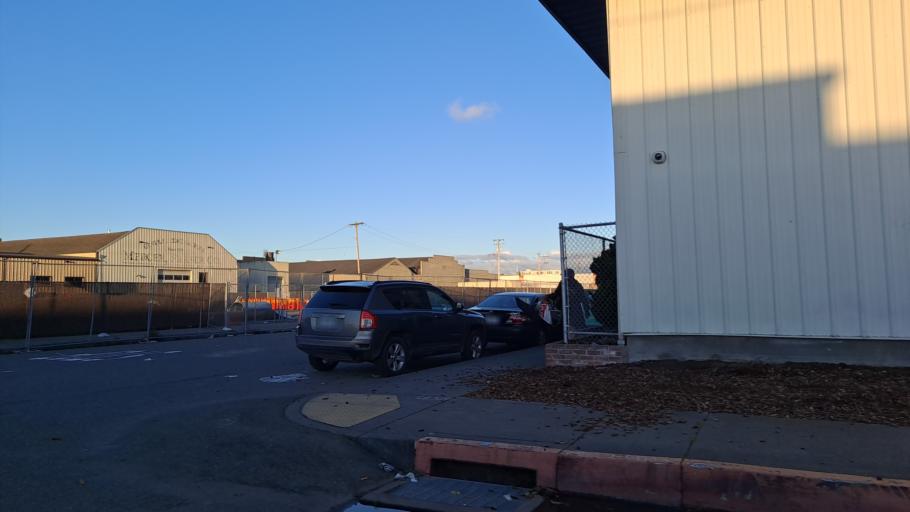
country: US
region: California
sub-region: Humboldt County
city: Eureka
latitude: 40.8024
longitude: -124.1738
